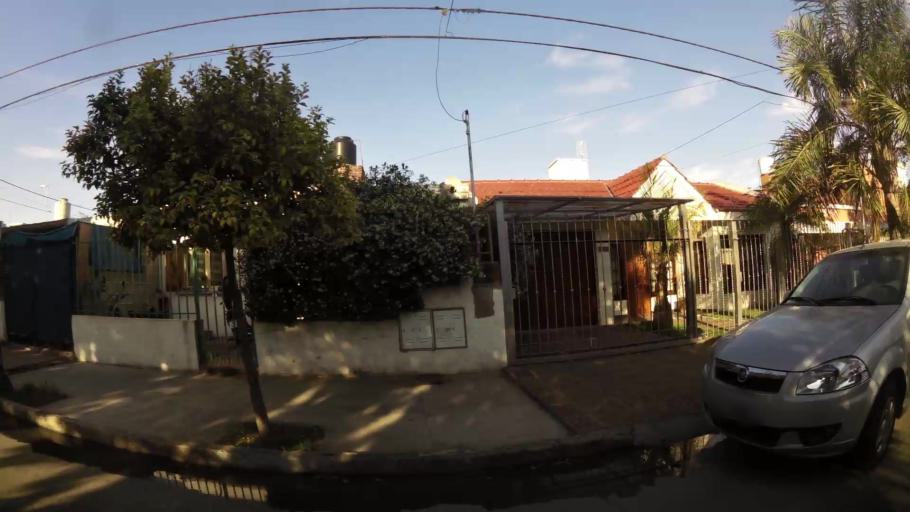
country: AR
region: Cordoba
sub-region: Departamento de Capital
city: Cordoba
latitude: -31.3924
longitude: -64.2167
